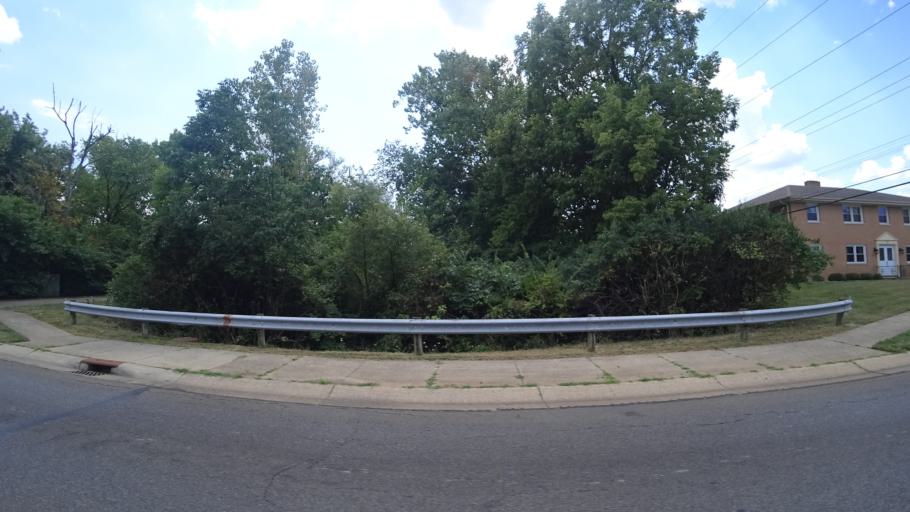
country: US
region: Ohio
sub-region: Butler County
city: Hamilton
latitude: 39.4237
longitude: -84.5623
